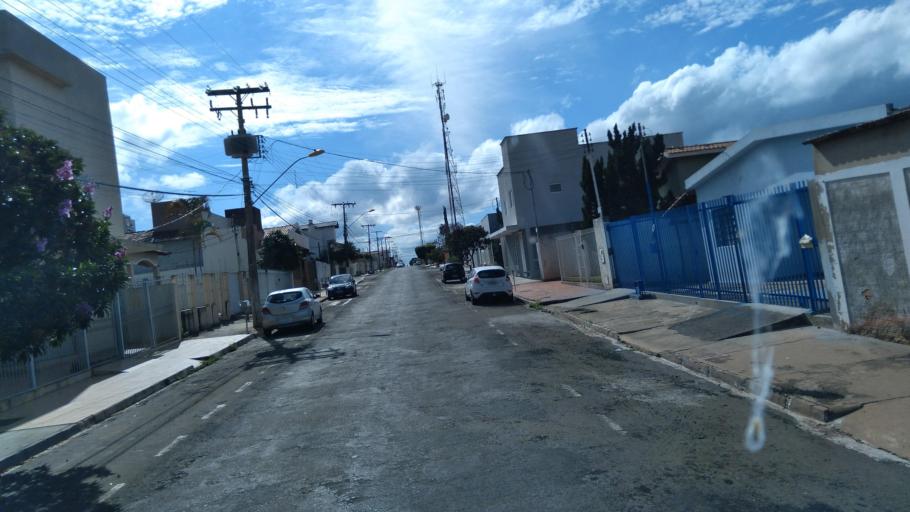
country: BR
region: Goias
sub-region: Mineiros
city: Mineiros
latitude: -17.5631
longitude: -52.5565
